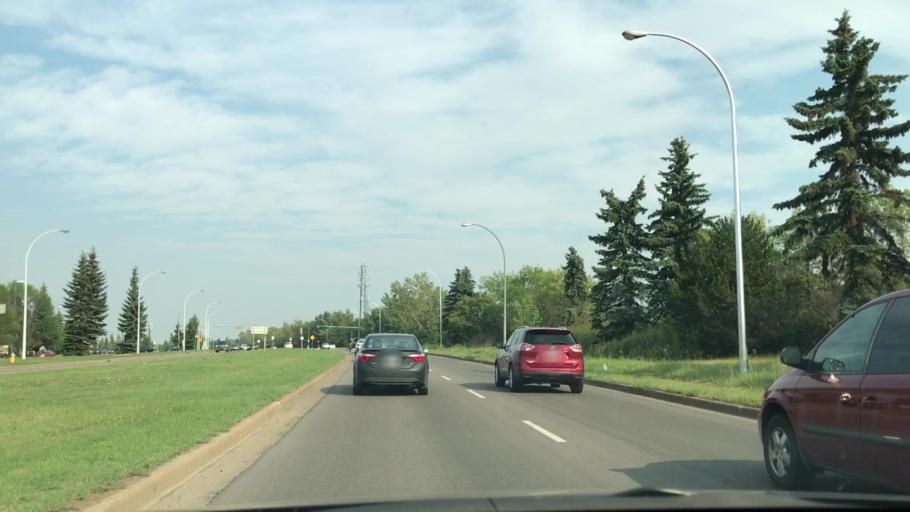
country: CA
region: Alberta
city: Edmonton
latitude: 53.4528
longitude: -113.4773
